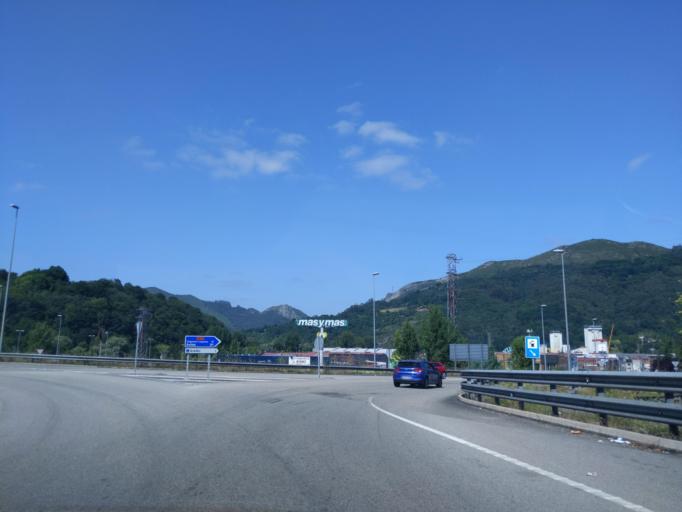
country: ES
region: Asturias
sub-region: Province of Asturias
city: Sama
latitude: 43.3222
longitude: -5.7172
